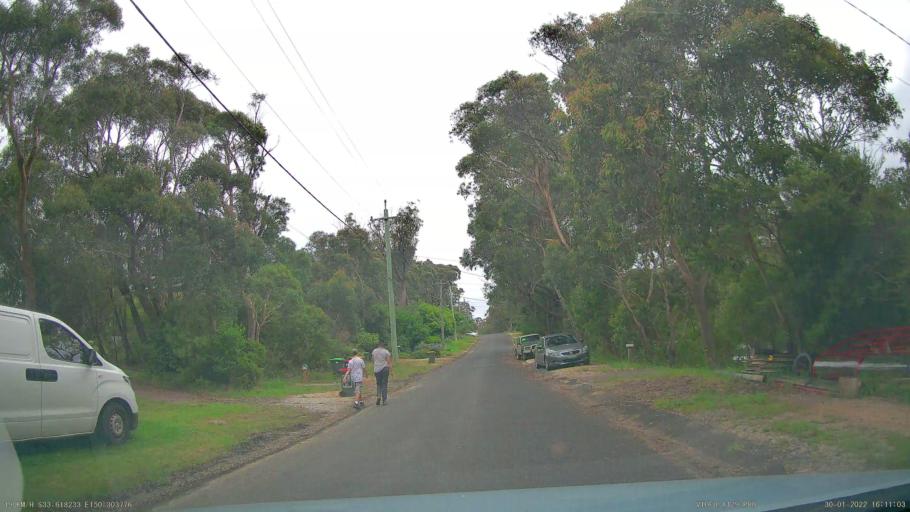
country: AU
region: New South Wales
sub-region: Blue Mountains Municipality
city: Blackheath
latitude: -33.6183
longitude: 150.3037
